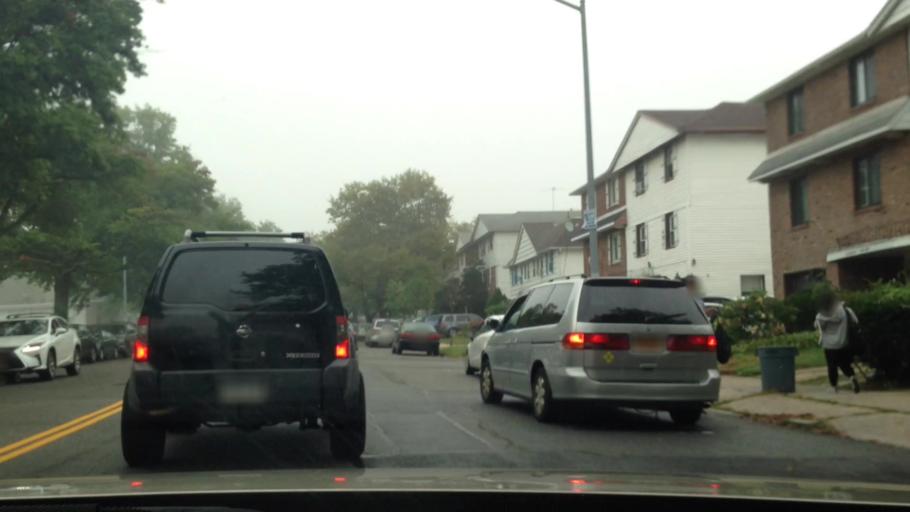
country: US
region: New York
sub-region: Nassau County
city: East Atlantic Beach
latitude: 40.7541
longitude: -73.7560
